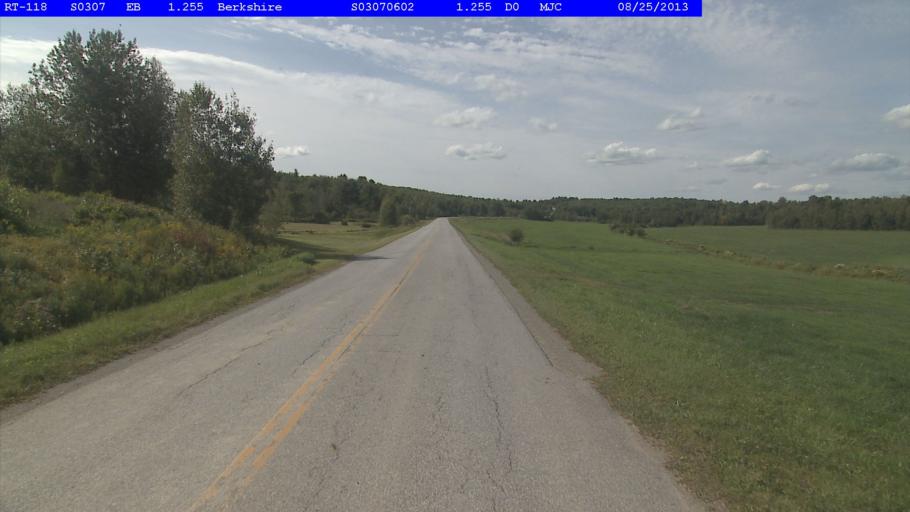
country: US
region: Vermont
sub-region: Franklin County
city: Enosburg Falls
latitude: 44.9395
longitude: -72.7345
